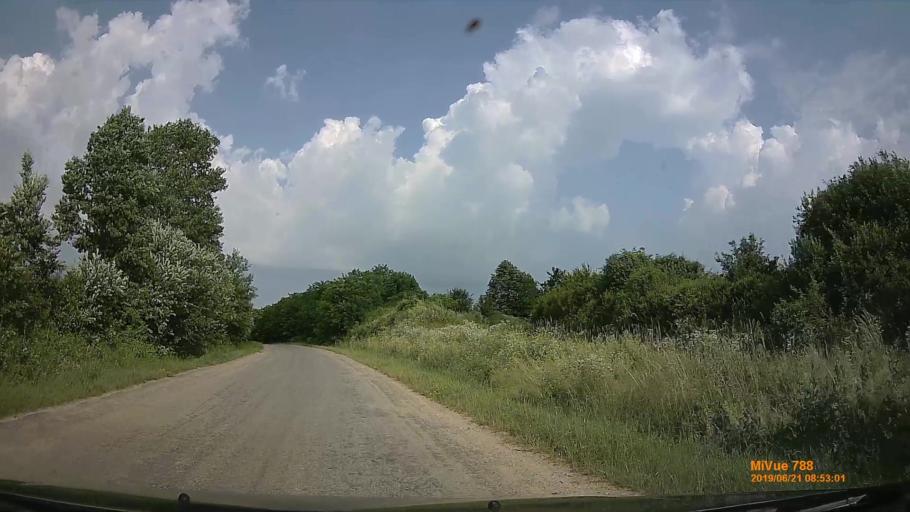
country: HU
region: Baranya
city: Buekkoesd
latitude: 46.1698
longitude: 17.8951
